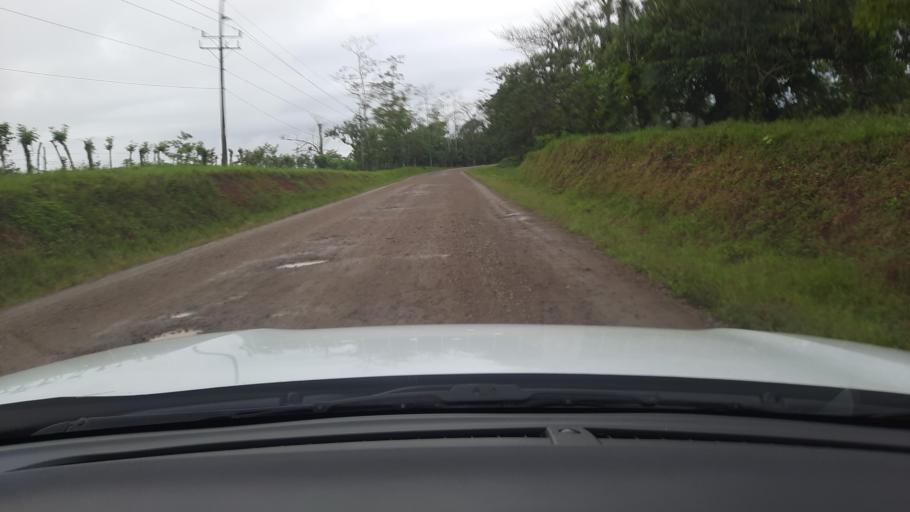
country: CR
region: Alajuela
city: San Jose
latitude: 10.9904
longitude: -85.2753
